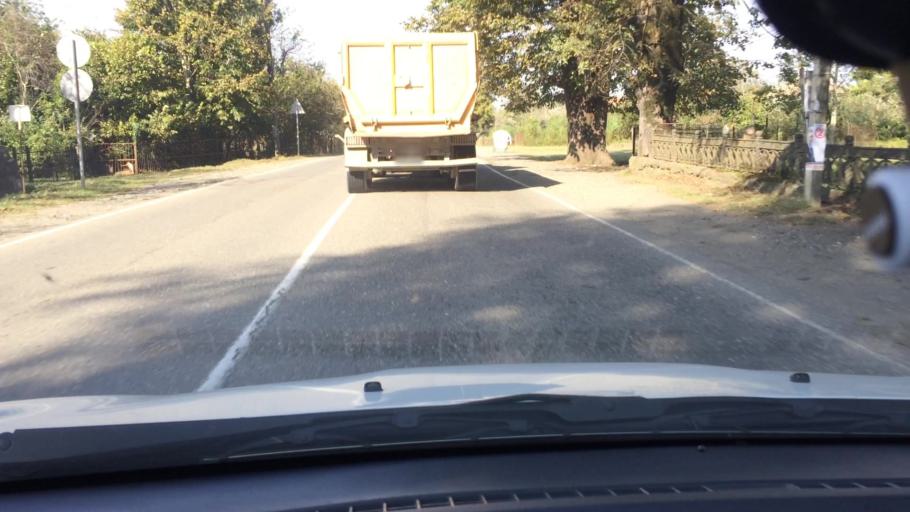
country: GE
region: Guria
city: Lanchkhuti
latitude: 42.0840
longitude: 41.9824
